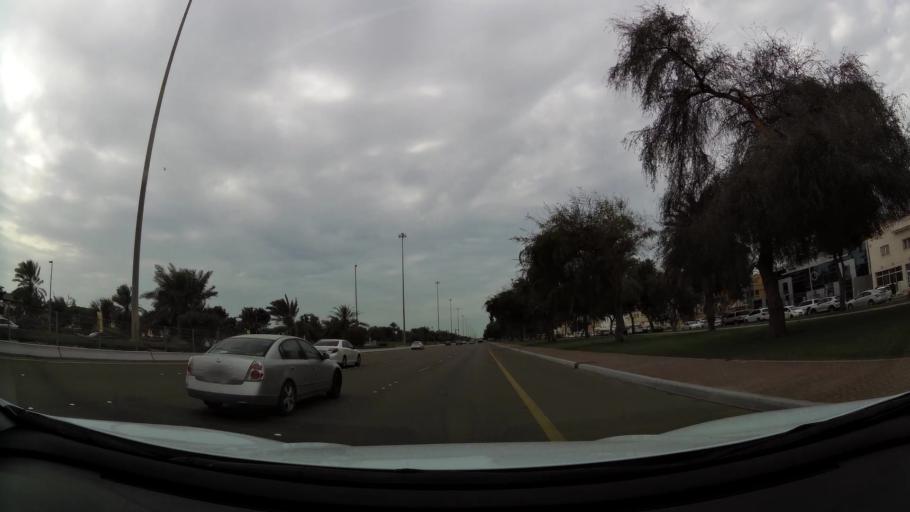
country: AE
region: Abu Dhabi
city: Abu Dhabi
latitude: 24.4257
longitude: 54.4060
